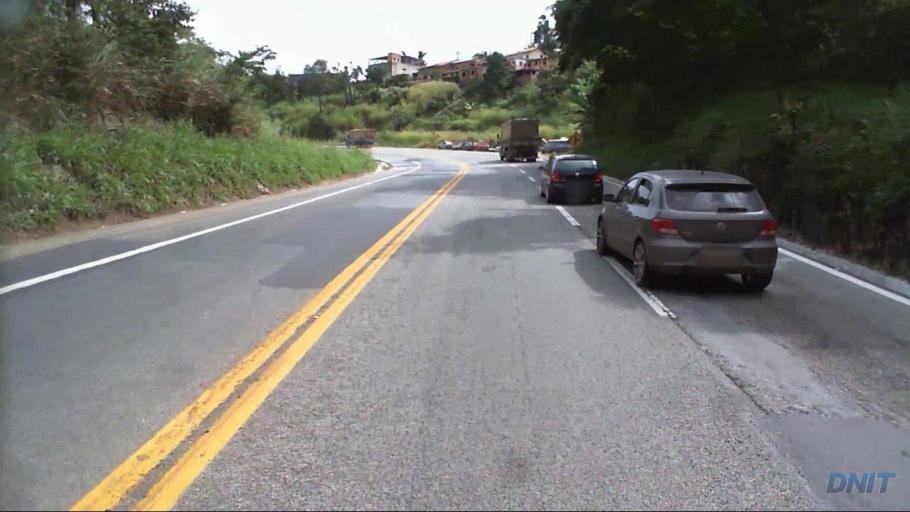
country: BR
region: Minas Gerais
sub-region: Caete
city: Caete
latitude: -19.7234
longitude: -43.5798
